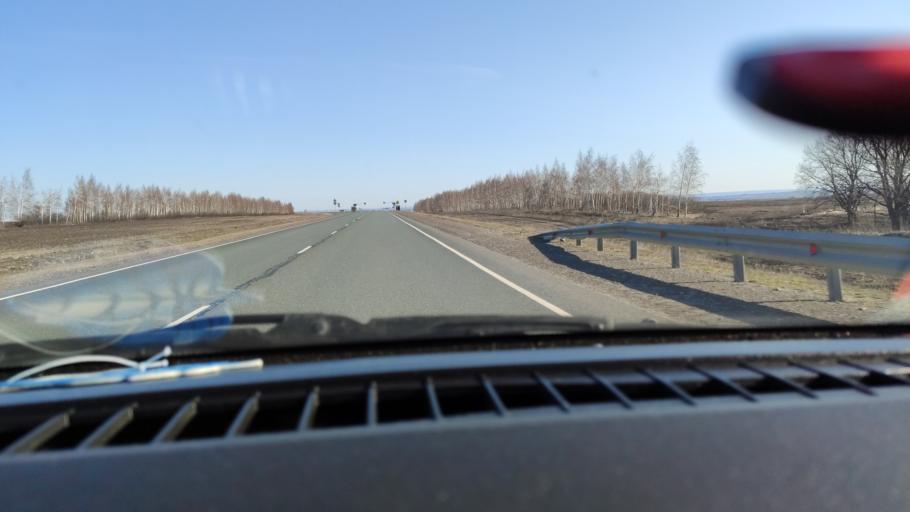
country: RU
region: Samara
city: Syzran'
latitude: 52.9495
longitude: 48.3055
